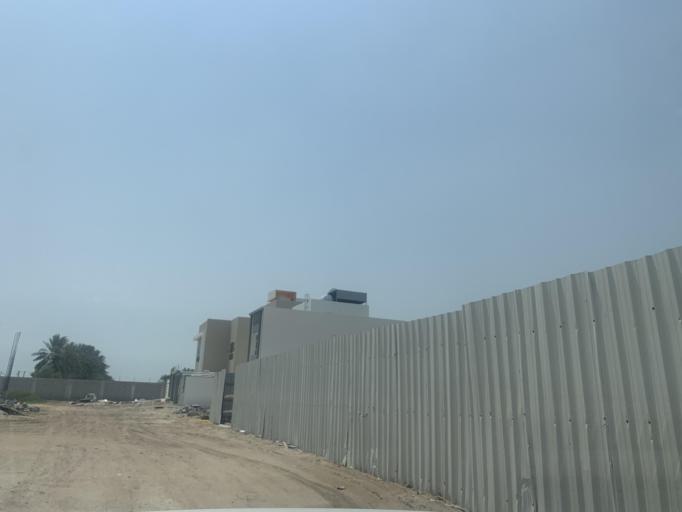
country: BH
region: Central Governorate
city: Madinat Hamad
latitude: 26.1301
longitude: 50.4653
